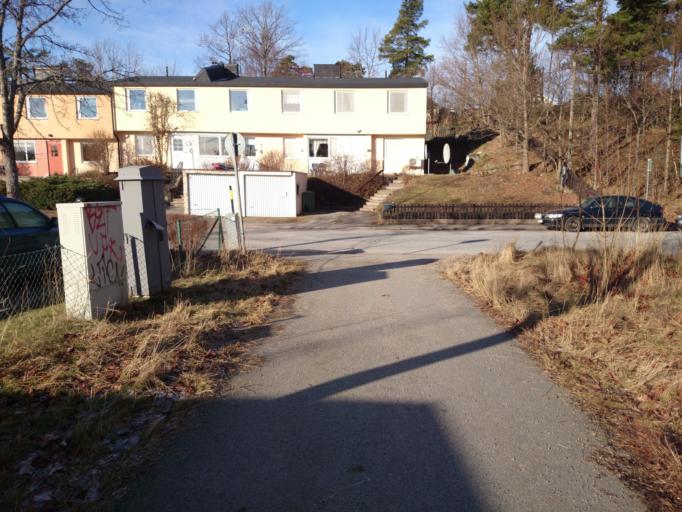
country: SE
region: Stockholm
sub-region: Nynashamns Kommun
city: Nynashamn
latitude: 58.8945
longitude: 17.9280
